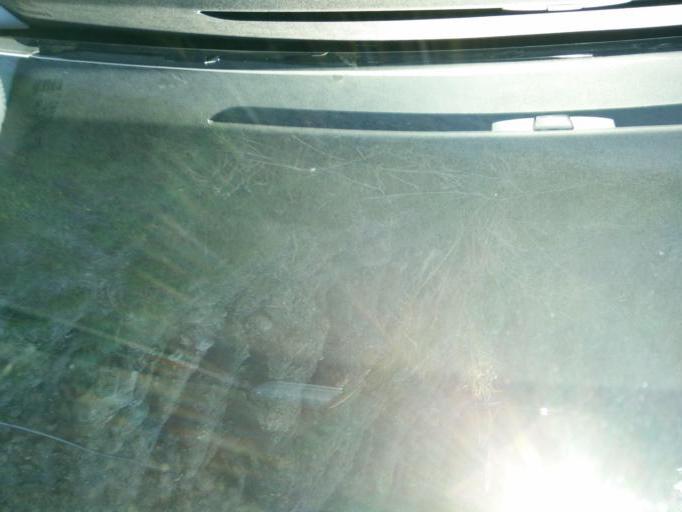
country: GR
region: Crete
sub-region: Nomos Lasithiou
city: Gra Liyia
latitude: 34.9993
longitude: 25.5164
